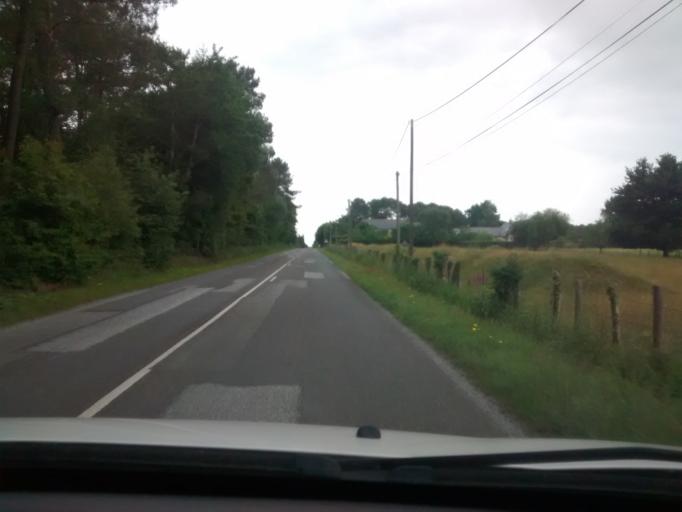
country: FR
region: Brittany
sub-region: Departement d'Ille-et-Vilaine
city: La Bouexiere
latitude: 48.1620
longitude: -1.4402
